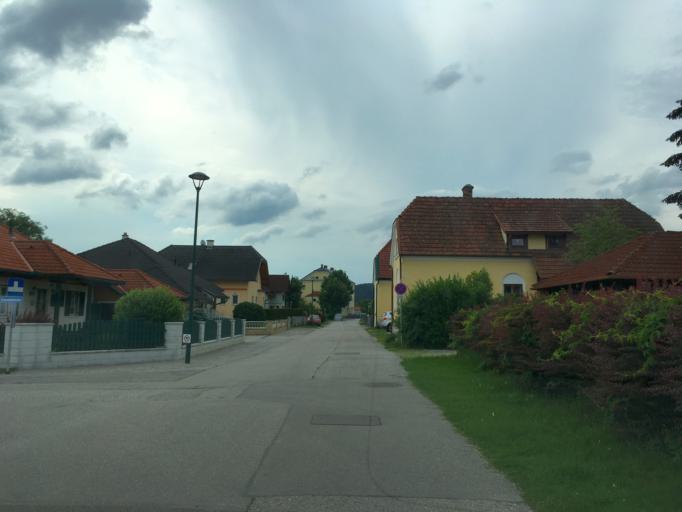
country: AT
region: Lower Austria
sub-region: Politischer Bezirk Wiener Neustadt
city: Bad Erlach
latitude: 47.7307
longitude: 16.2160
